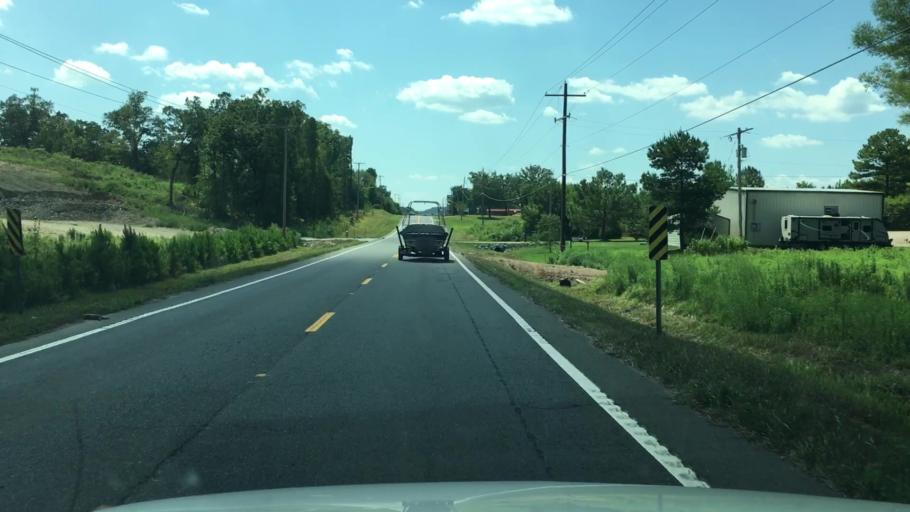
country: US
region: Arkansas
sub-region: Garland County
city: Piney
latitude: 34.5105
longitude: -93.2106
